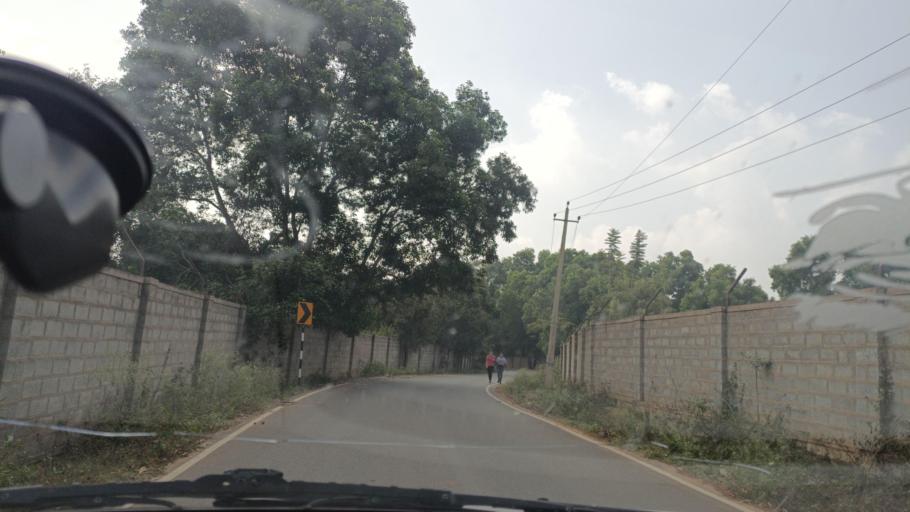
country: IN
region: Karnataka
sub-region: Bangalore Urban
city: Yelahanka
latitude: 13.1507
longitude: 77.6067
